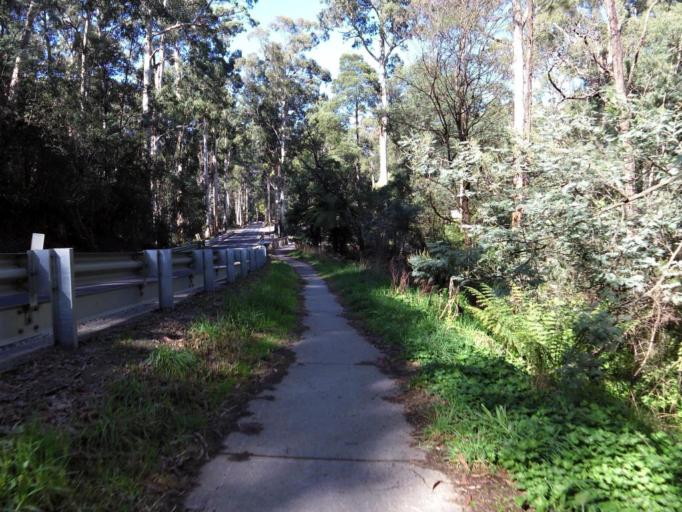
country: AU
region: Victoria
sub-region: Cardinia
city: Cockatoo
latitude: -37.9414
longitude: 145.4929
